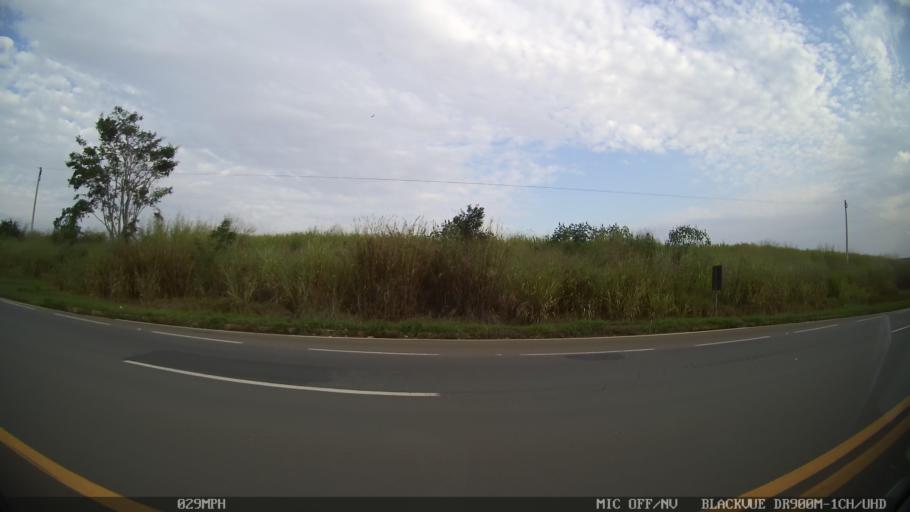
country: BR
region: Sao Paulo
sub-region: Cosmopolis
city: Cosmopolis
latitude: -22.6280
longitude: -47.2726
